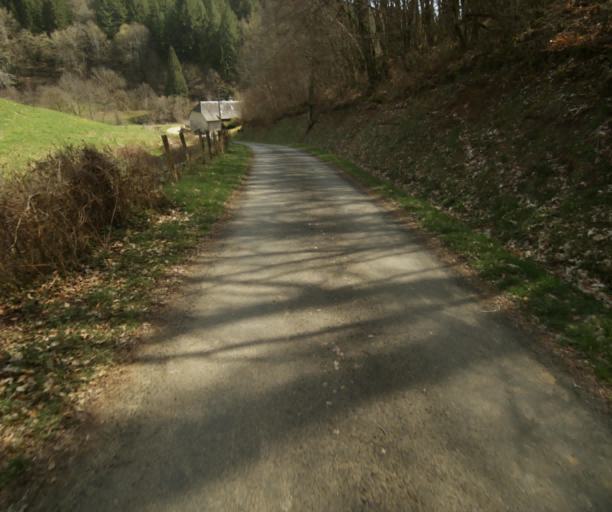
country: FR
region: Limousin
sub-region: Departement de la Correze
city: Naves
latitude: 45.3716
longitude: 1.7862
